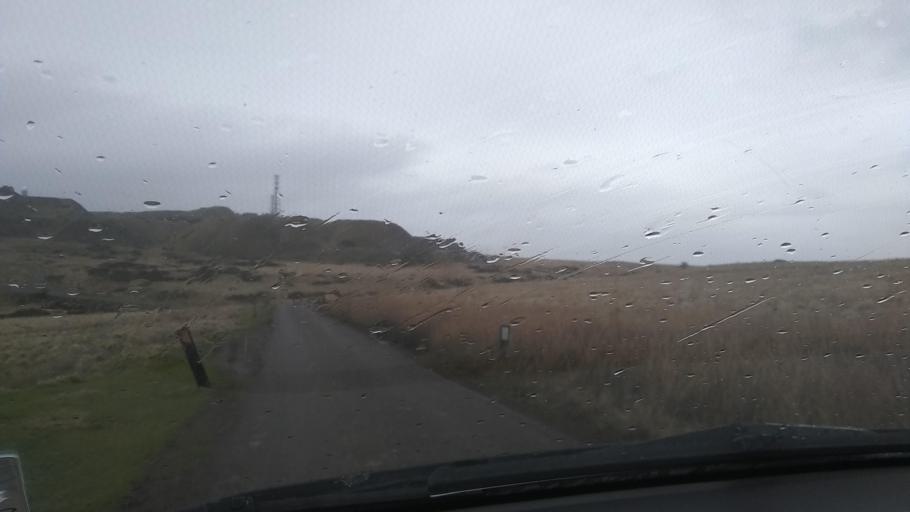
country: GB
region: England
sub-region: Worcestershire
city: Tenbury Wells
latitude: 52.3906
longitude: -2.5961
